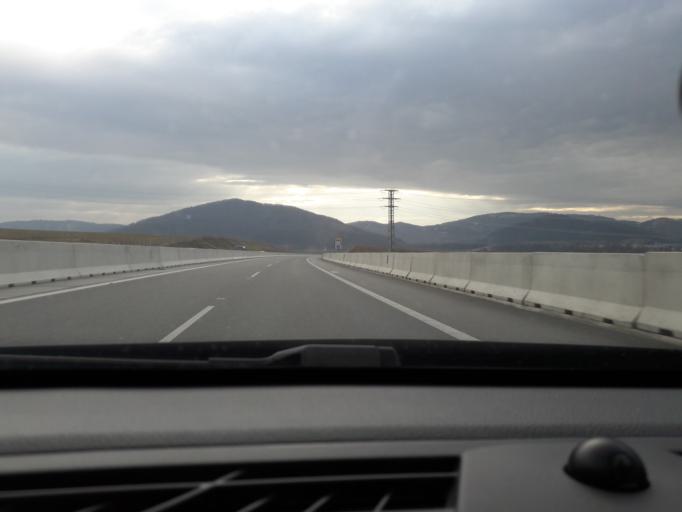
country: SK
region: Banskobystricky
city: Hrochot,Slovakia
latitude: 48.5677
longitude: 19.3055
